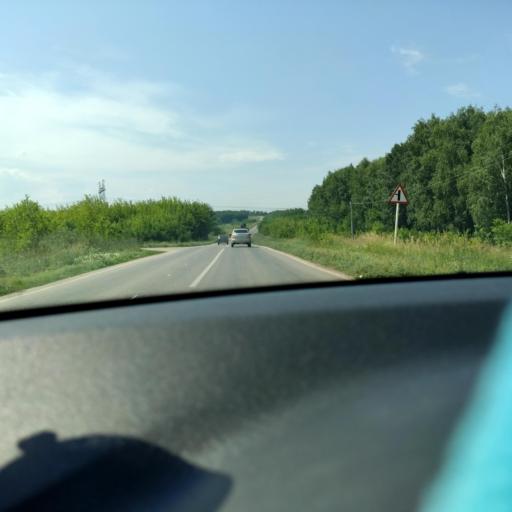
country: RU
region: Samara
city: Petra-Dubrava
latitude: 53.3453
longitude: 50.5137
